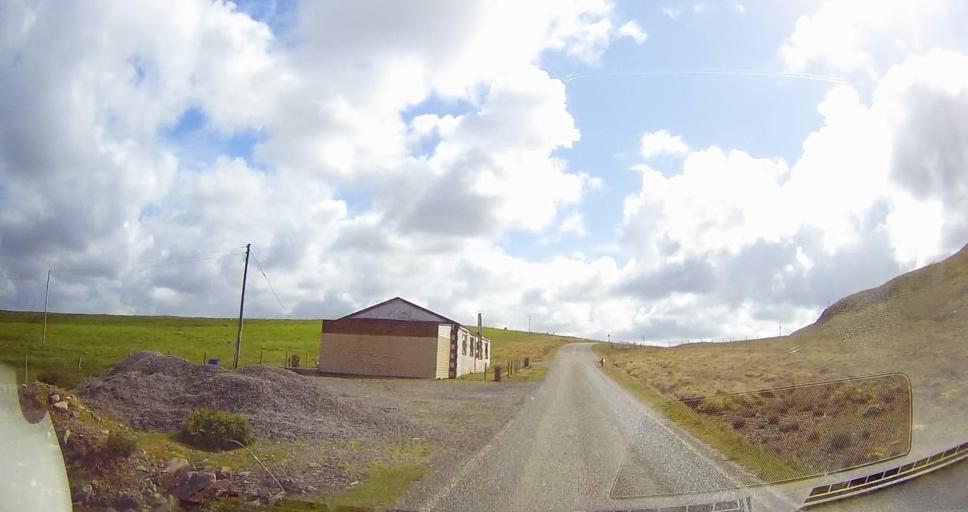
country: GB
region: Scotland
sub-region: Shetland Islands
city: Lerwick
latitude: 60.5451
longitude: -1.3413
